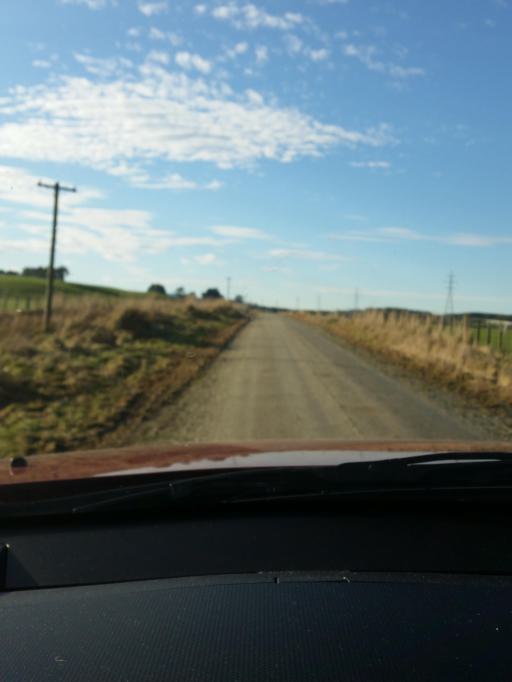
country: NZ
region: Southland
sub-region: Gore District
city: Gore
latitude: -46.2179
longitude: 168.7529
